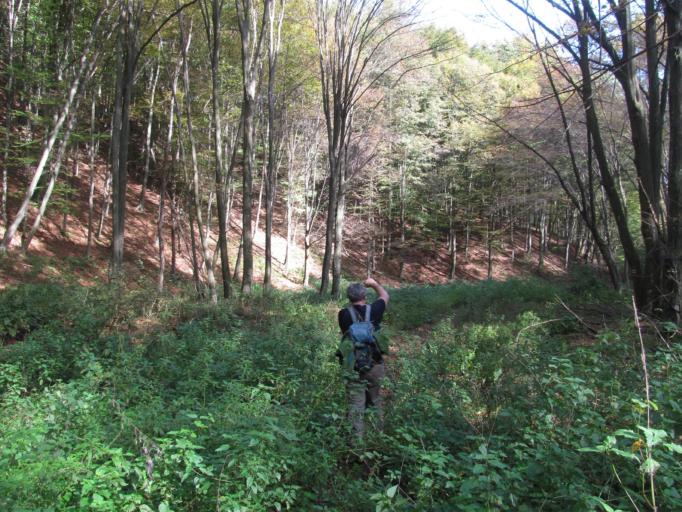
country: HU
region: Veszprem
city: Herend
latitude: 47.2766
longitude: 17.6983
